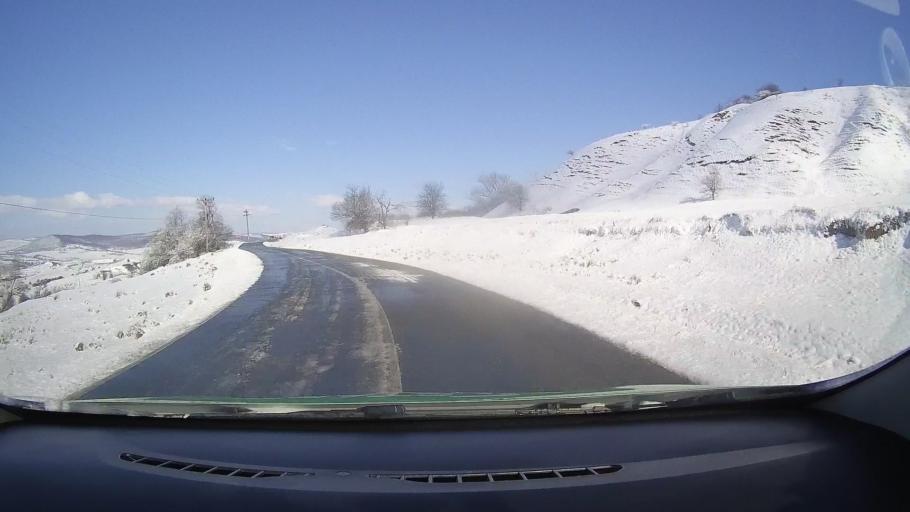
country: RO
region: Sibiu
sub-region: Comuna Rosia
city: Rosia
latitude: 45.7866
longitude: 24.3739
